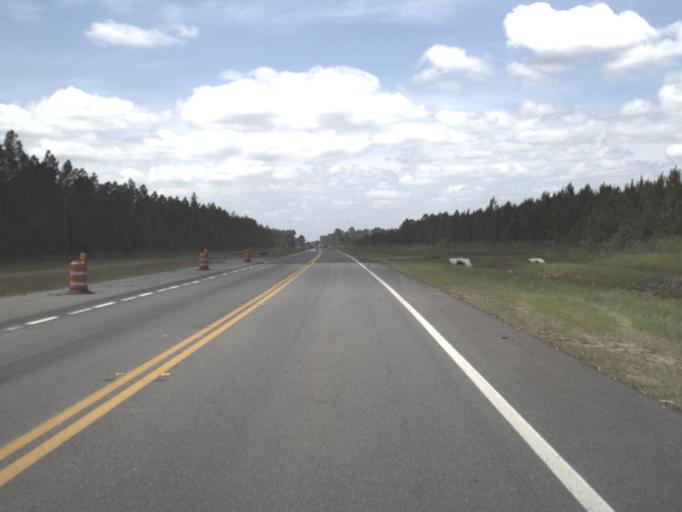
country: US
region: Florida
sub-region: Duval County
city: Baldwin
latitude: 30.3728
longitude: -81.9434
